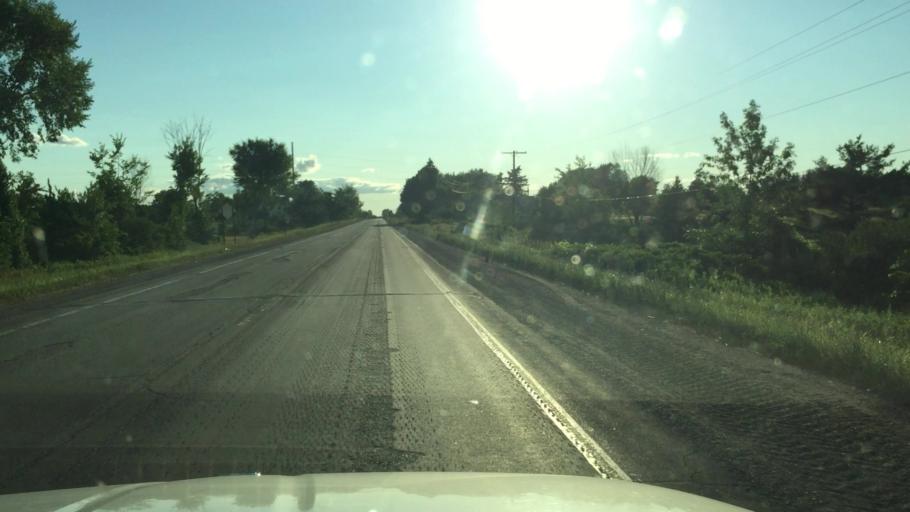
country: US
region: Michigan
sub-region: Lapeer County
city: Imlay City
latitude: 43.0252
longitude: -83.0096
